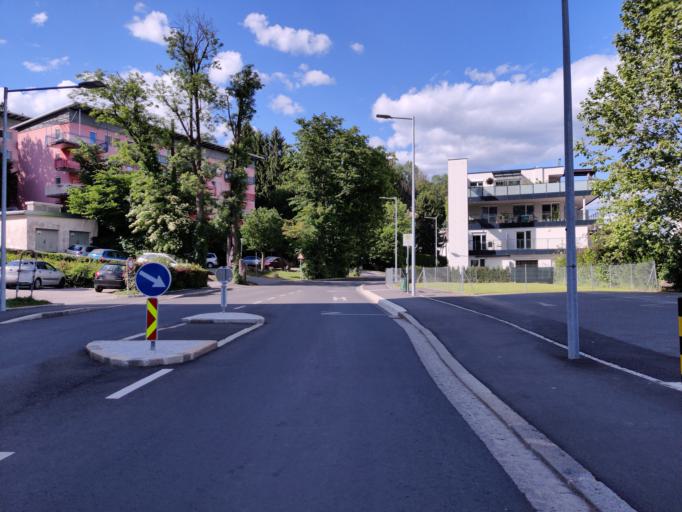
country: AT
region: Styria
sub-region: Graz Stadt
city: Wetzelsdorf
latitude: 47.0479
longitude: 15.3877
